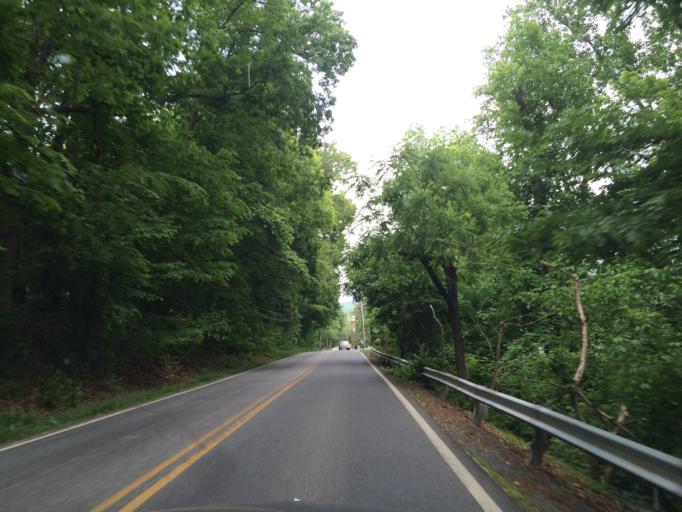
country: US
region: Maryland
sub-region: Howard County
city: Columbia
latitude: 39.2680
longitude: -76.9182
